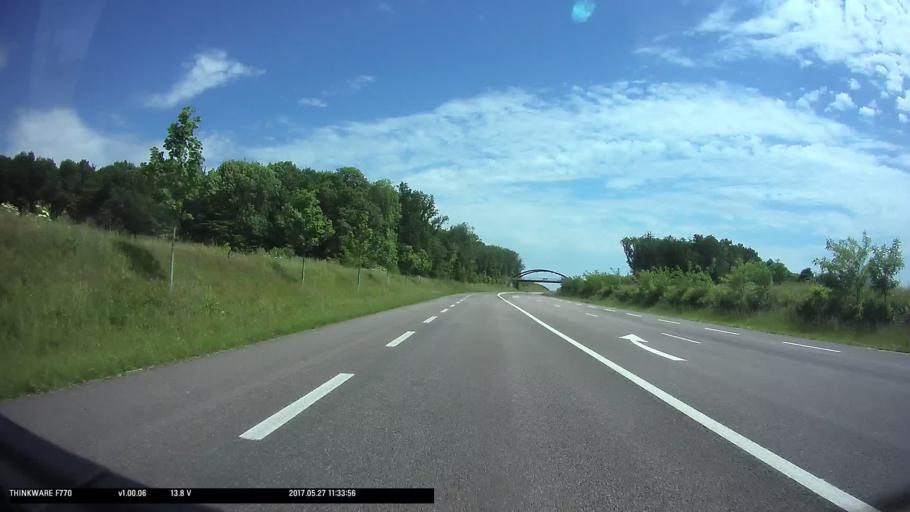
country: FR
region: Haute-Normandie
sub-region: Departement de l'Eure
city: Gisors
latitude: 49.2874
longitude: 1.7596
